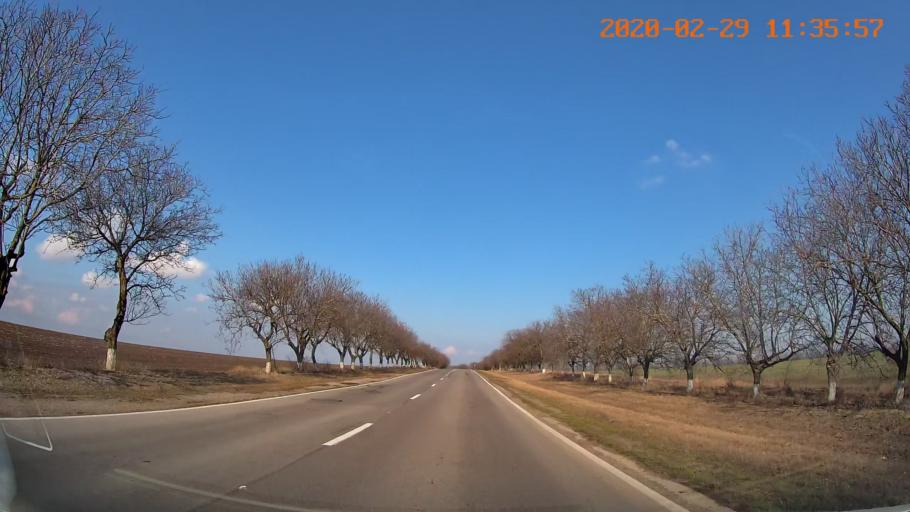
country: MD
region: Rezina
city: Saharna
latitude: 47.5884
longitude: 29.0599
